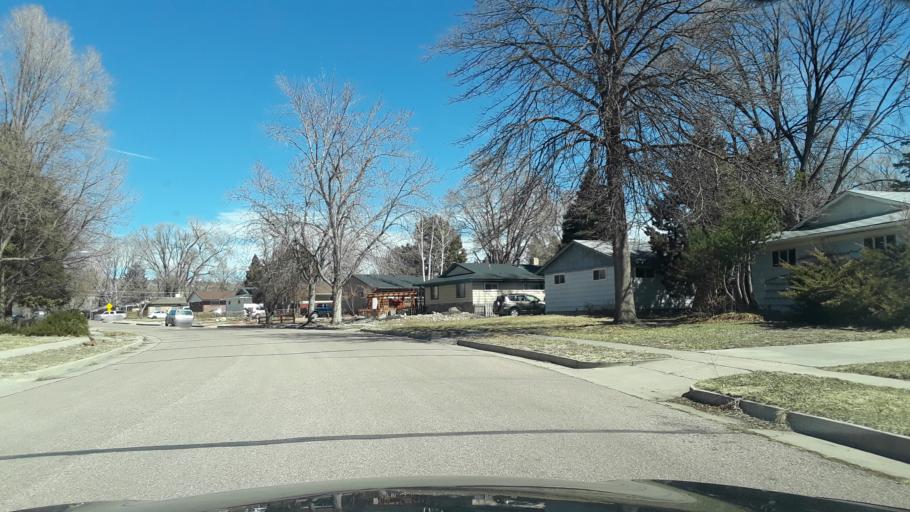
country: US
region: Colorado
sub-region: El Paso County
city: Colorado Springs
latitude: 38.8706
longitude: -104.8058
